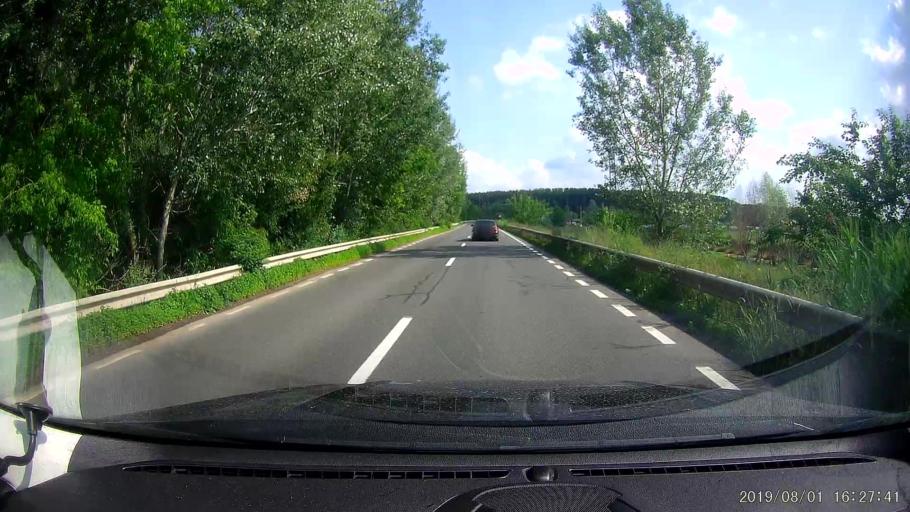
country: RO
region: Calarasi
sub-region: Municipiul Calarasi
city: Calarasi
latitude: 44.1604
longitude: 27.3163
